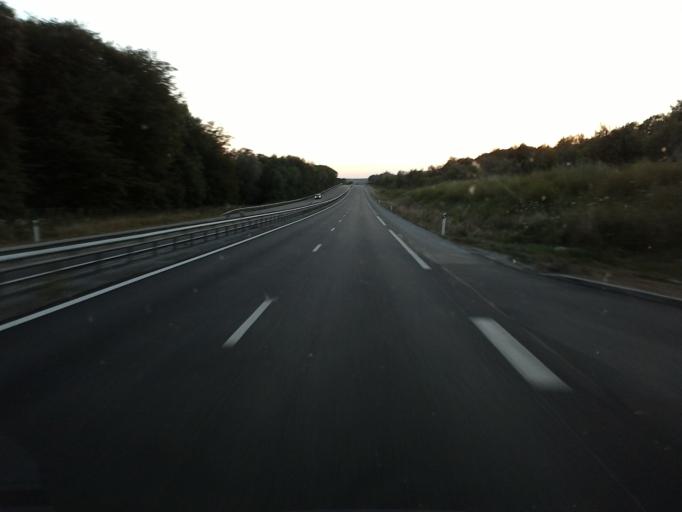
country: FR
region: Franche-Comte
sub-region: Departement du Jura
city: Poligny
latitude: 46.8414
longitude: 5.6666
